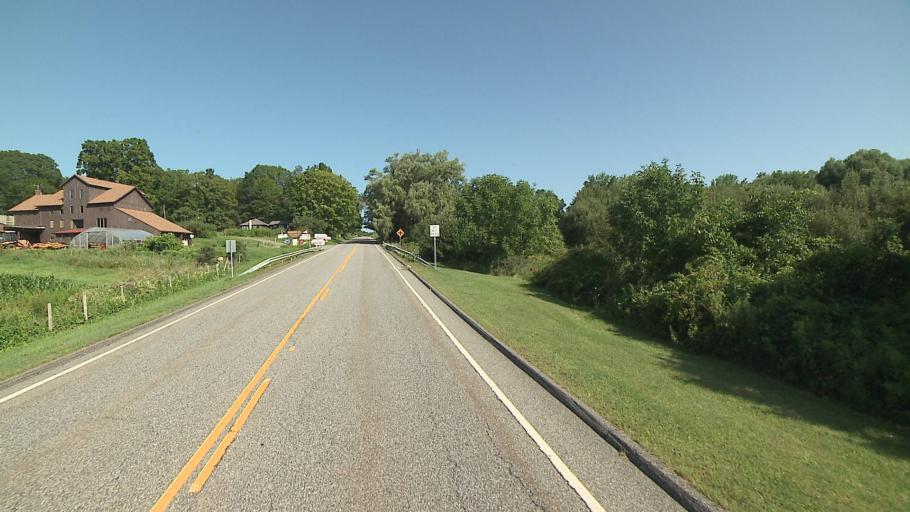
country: US
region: Connecticut
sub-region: Litchfield County
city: Kent
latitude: 41.8293
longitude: -73.4250
